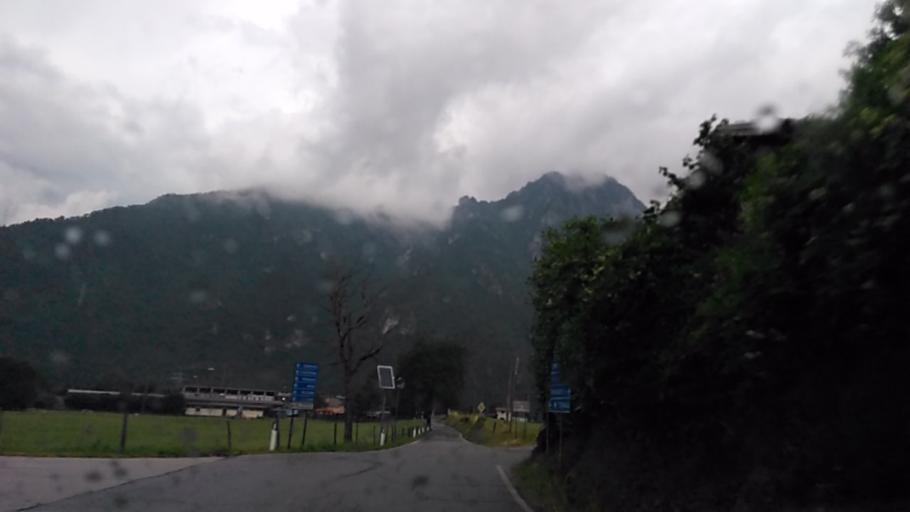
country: IT
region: Lombardy
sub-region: Provincia di Brescia
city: Pieve
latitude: 45.7826
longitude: 10.7254
